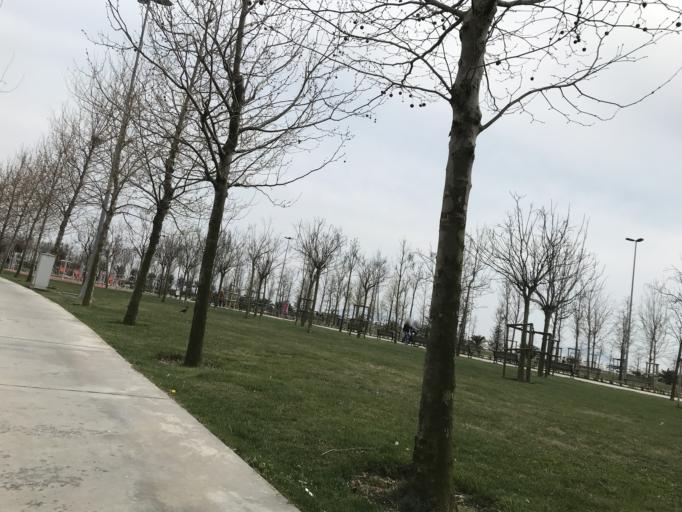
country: TR
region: Istanbul
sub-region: Atasehir
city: Atasehir
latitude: 40.9391
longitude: 29.1083
